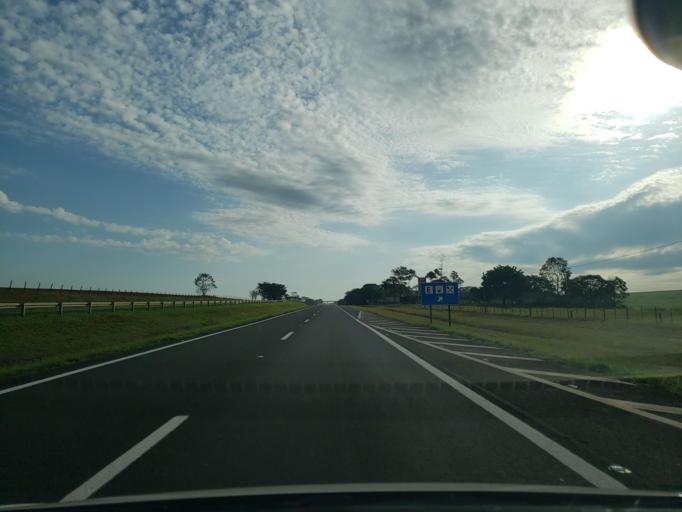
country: BR
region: Sao Paulo
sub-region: Valparaiso
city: Valparaiso
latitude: -21.2060
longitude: -50.7750
